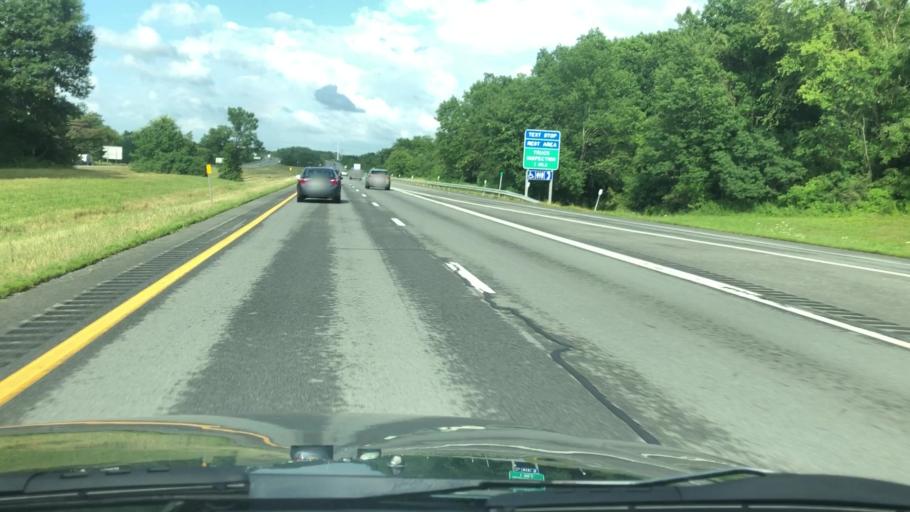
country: US
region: New York
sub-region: Orange County
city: Middletown
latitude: 41.4178
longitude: -74.4166
